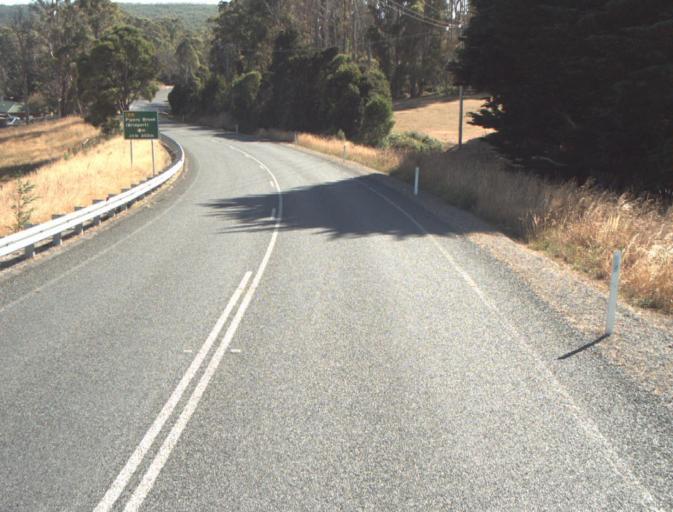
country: AU
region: Tasmania
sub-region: Dorset
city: Bridport
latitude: -41.1650
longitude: 147.2397
